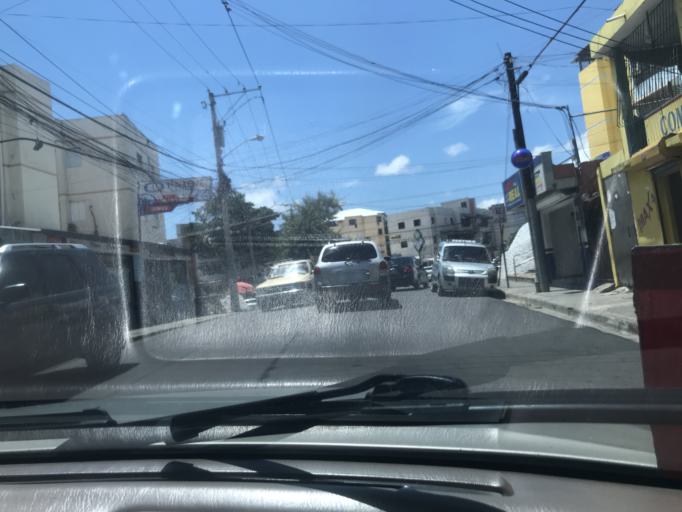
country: DO
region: Santiago
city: Santiago de los Caballeros
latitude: 19.4298
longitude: -70.6948
